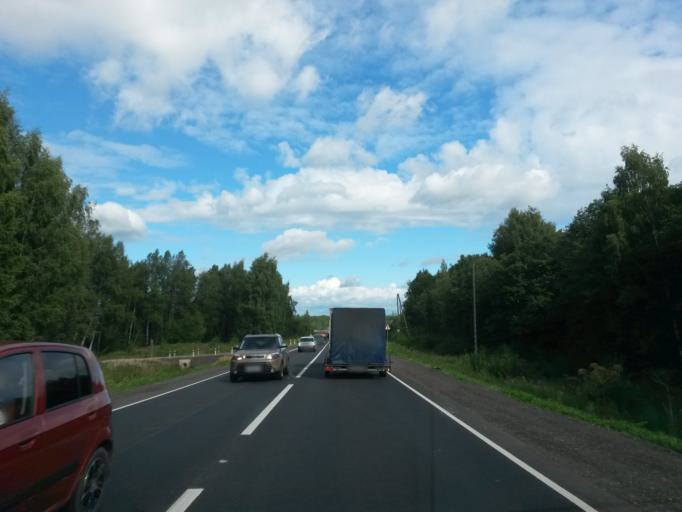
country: RU
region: Jaroslavl
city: Yaroslavl
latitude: 57.5044
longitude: 39.8985
